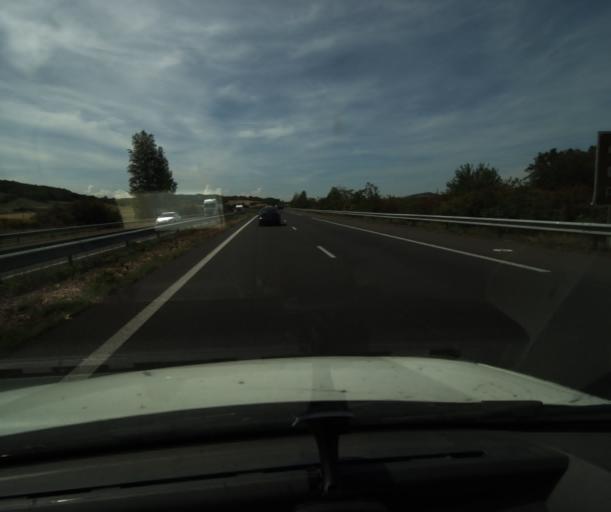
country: FR
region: Languedoc-Roussillon
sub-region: Departement de l'Aude
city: Villeneuve-la-Comptal
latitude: 43.3245
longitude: 1.8571
